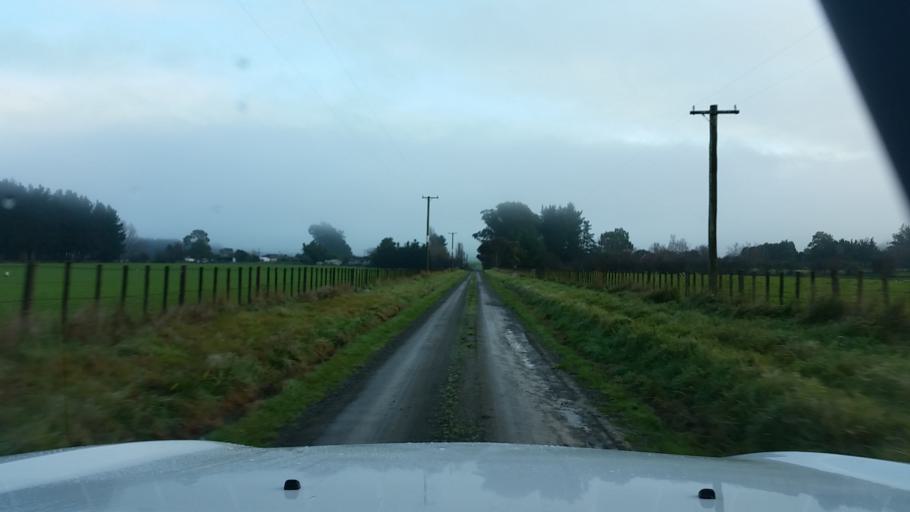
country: NZ
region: Wellington
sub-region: Masterton District
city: Masterton
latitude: -41.0807
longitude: 175.6601
